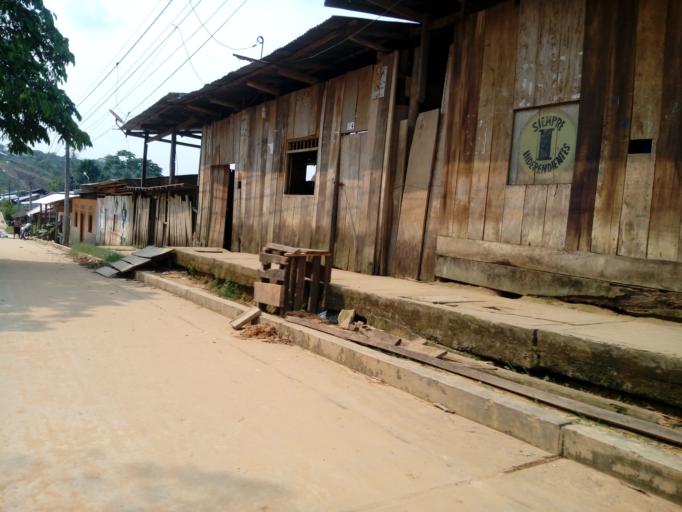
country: PE
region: Loreto
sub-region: Provincia de Loreto
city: Nauta
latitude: -4.5005
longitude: -73.5822
